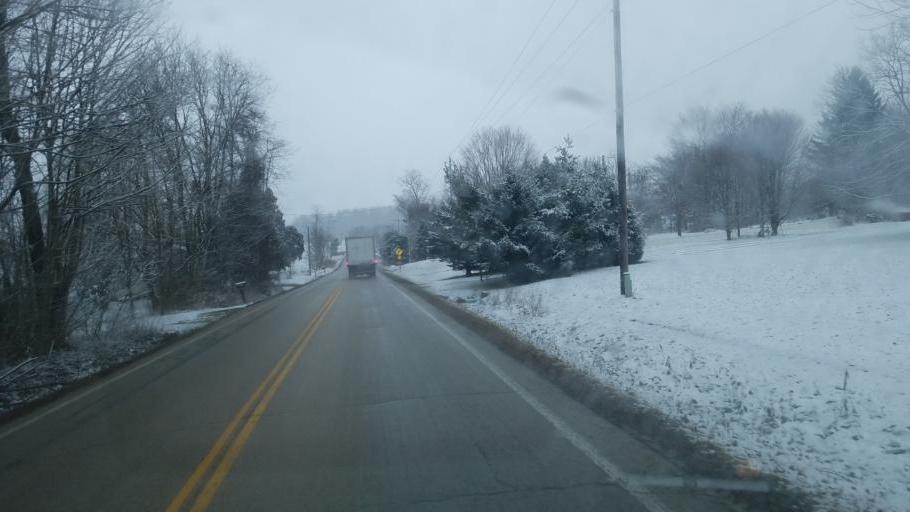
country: US
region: Ohio
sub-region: Portage County
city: Garrettsville
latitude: 41.3416
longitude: -81.0887
